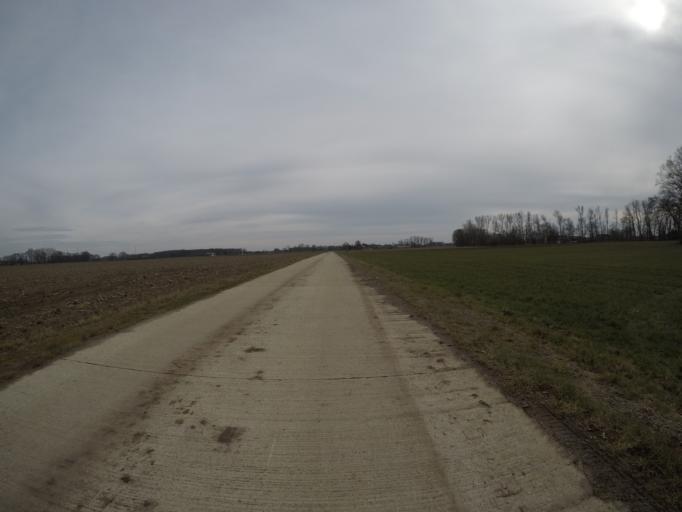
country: DE
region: North Rhine-Westphalia
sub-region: Regierungsbezirk Dusseldorf
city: Mehrhoog
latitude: 51.7879
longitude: 6.5442
